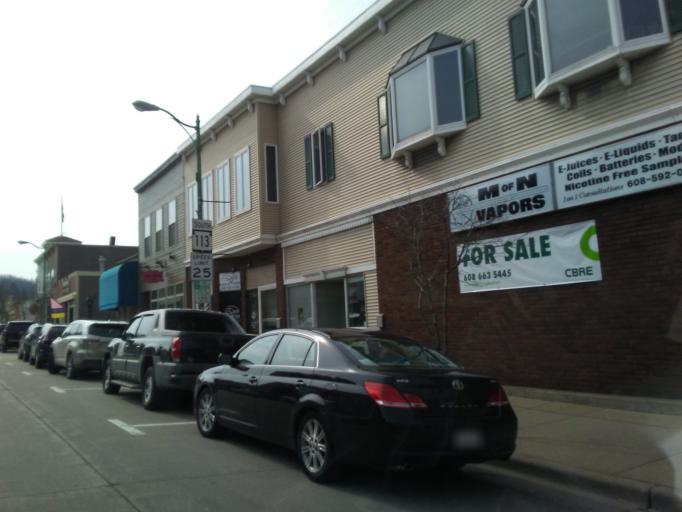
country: US
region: Wisconsin
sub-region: Columbia County
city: Lodi
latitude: 43.3138
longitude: -89.5266
